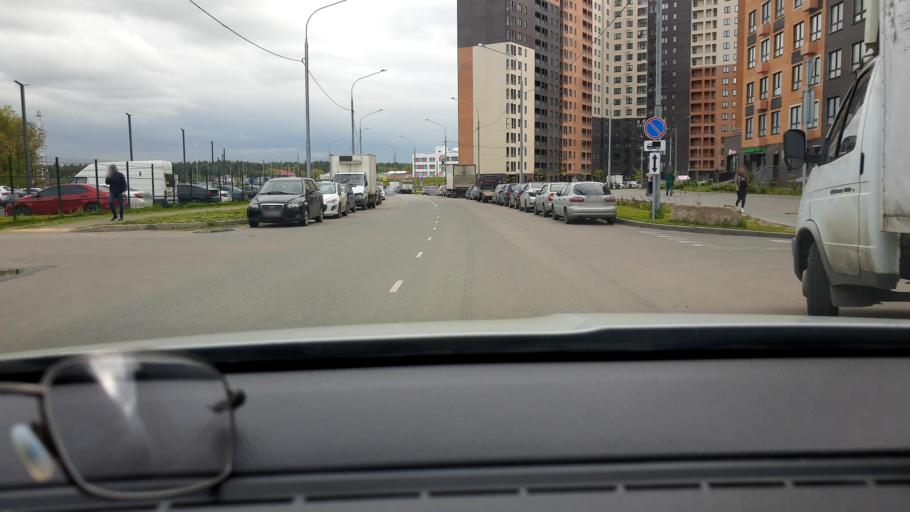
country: RU
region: Moscow
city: Annino
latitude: 55.5318
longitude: 37.6211
